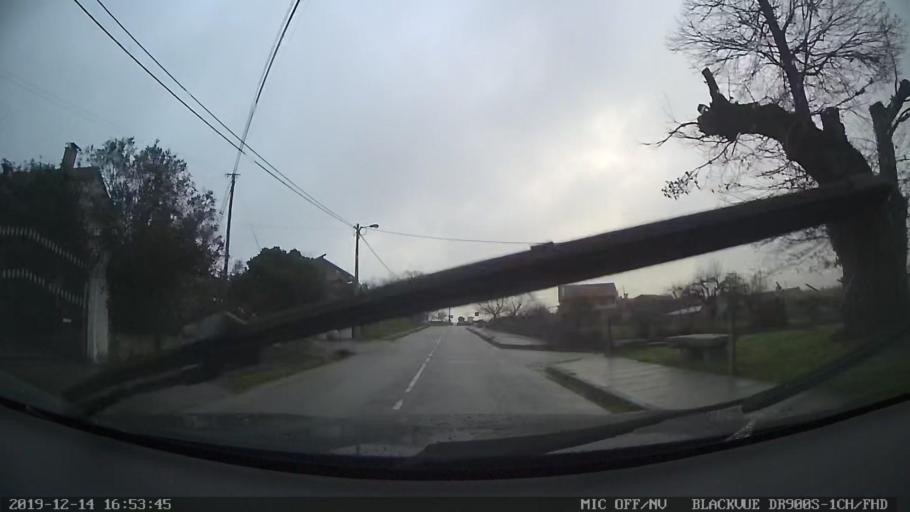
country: PT
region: Vila Real
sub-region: Murca
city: Murca
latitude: 41.4336
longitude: -7.5187
